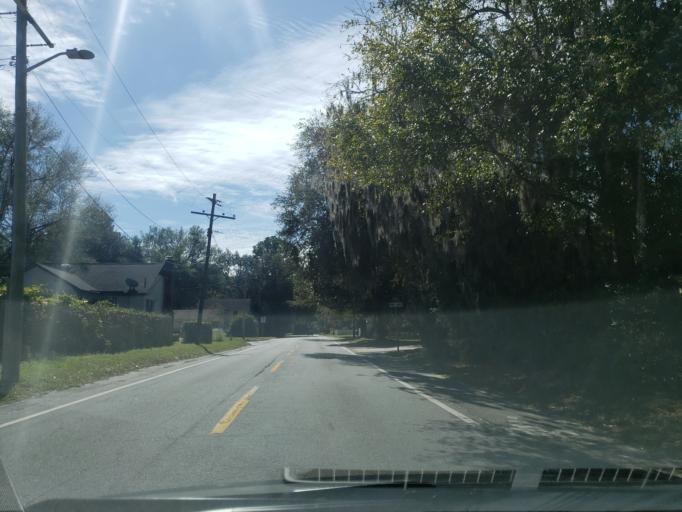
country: US
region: Georgia
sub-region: Chatham County
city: Thunderbolt
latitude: 32.0411
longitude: -81.0784
